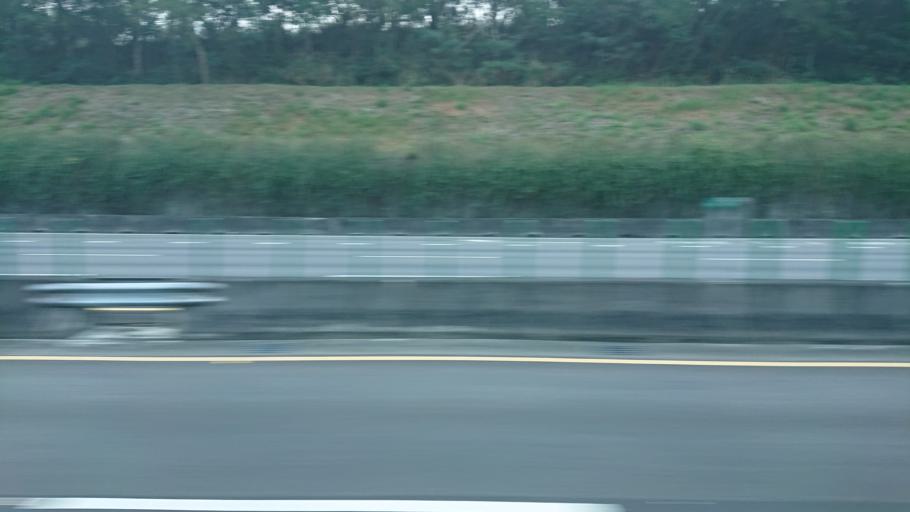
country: TW
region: Taiwan
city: Fengyuan
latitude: 24.3915
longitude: 120.7573
